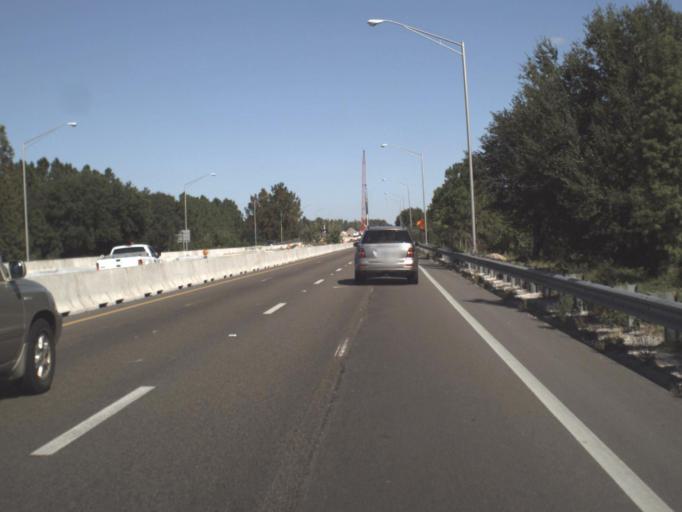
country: US
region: Florida
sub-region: Hillsborough County
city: Town 'n' Country
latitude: 28.0118
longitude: -82.5454
